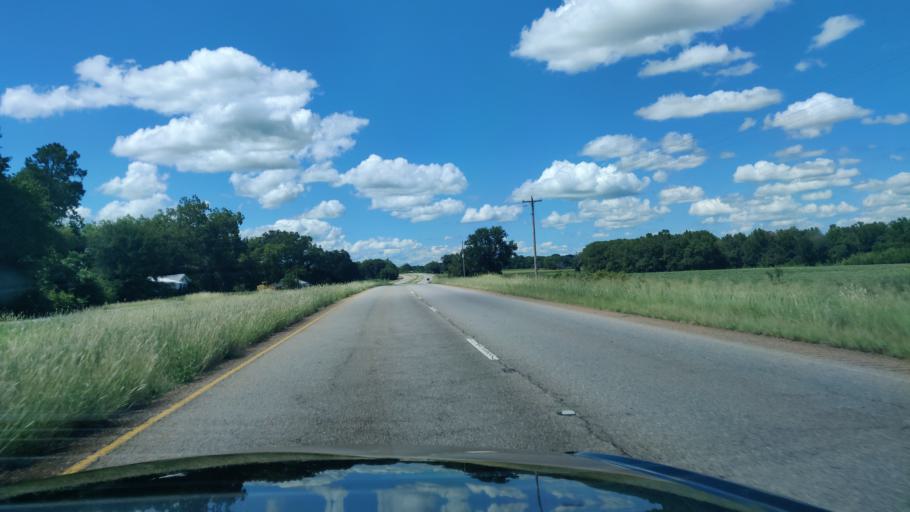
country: US
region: Georgia
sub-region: Stewart County
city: Richland
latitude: 32.0636
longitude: -84.6715
